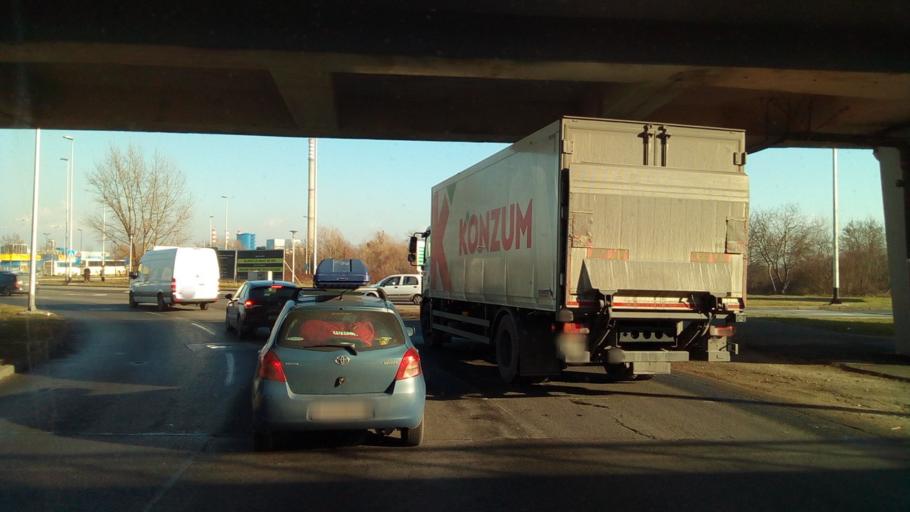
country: HR
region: Grad Zagreb
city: Novi Zagreb
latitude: 45.7776
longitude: 16.0022
